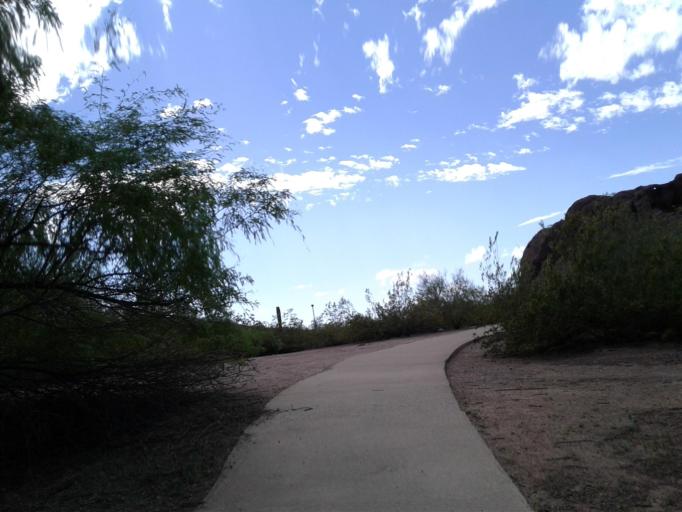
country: US
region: Arizona
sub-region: Maricopa County
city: Tempe Junction
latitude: 33.4562
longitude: -111.9427
